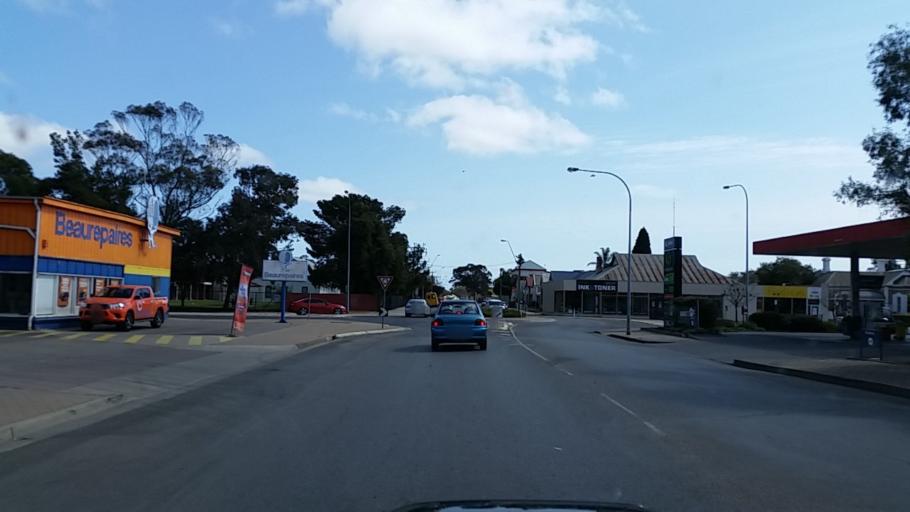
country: AU
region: South Australia
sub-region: Port Pirie City and Dists
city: Port Pirie
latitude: -33.1807
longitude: 138.0110
